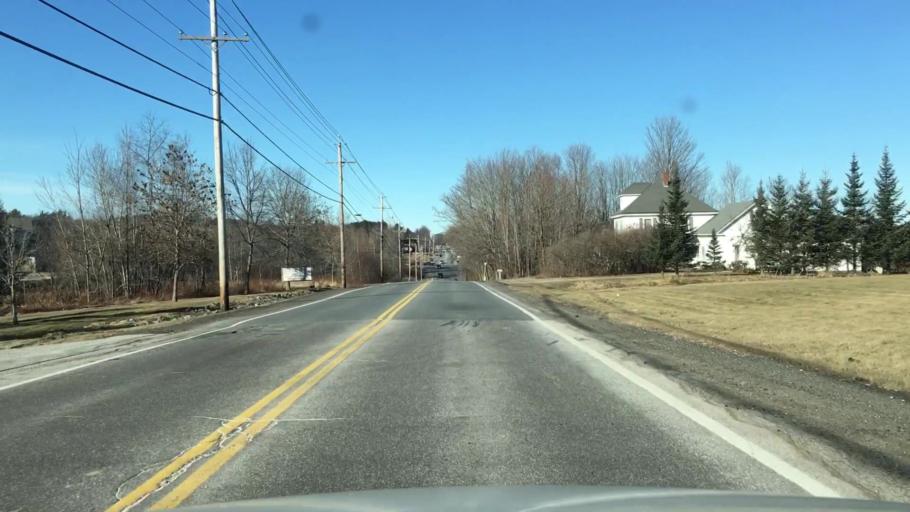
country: US
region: Maine
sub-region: Penobscot County
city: Bangor
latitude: 44.8219
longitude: -68.8057
